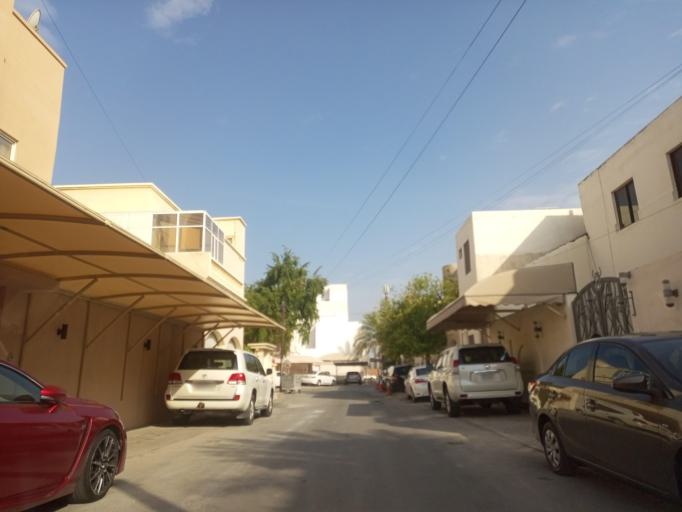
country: BH
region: Muharraq
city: Al Hadd
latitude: 26.2502
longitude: 50.6438
